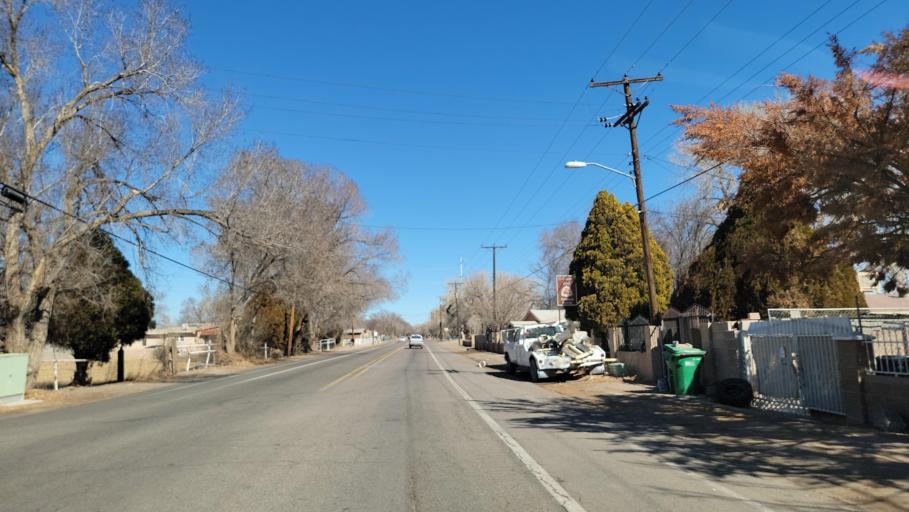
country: US
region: New Mexico
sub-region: Bernalillo County
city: South Valley
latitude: 35.0021
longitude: -106.6910
